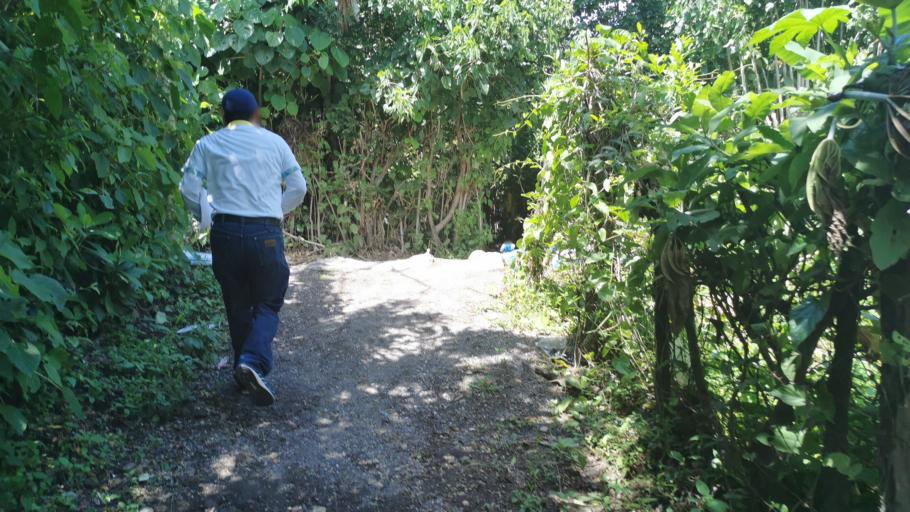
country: GT
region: Guatemala
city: Amatitlan
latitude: 14.4843
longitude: -90.6396
